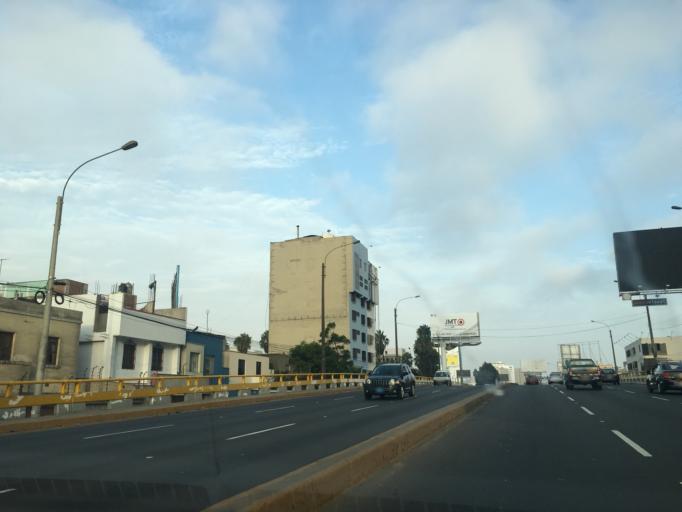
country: PE
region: Lima
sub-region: Lima
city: San Isidro
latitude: -12.0858
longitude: -77.0640
